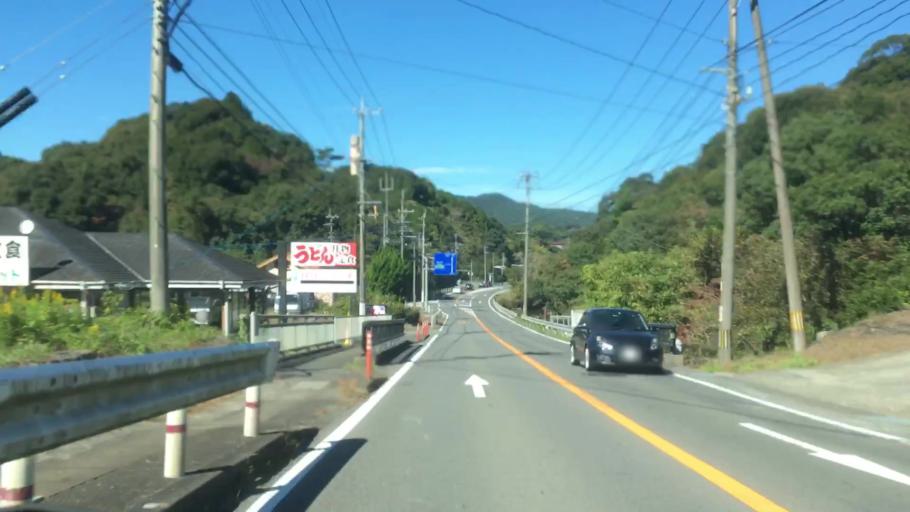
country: JP
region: Nagasaki
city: Sasebo
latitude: 32.9941
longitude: 129.7334
